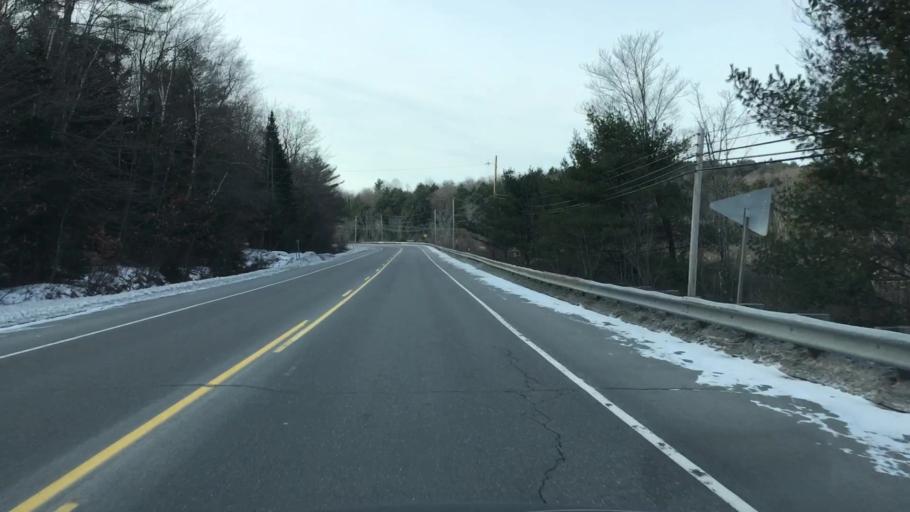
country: US
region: New Hampshire
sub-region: Sullivan County
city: Sunapee
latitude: 43.3783
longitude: -72.1141
